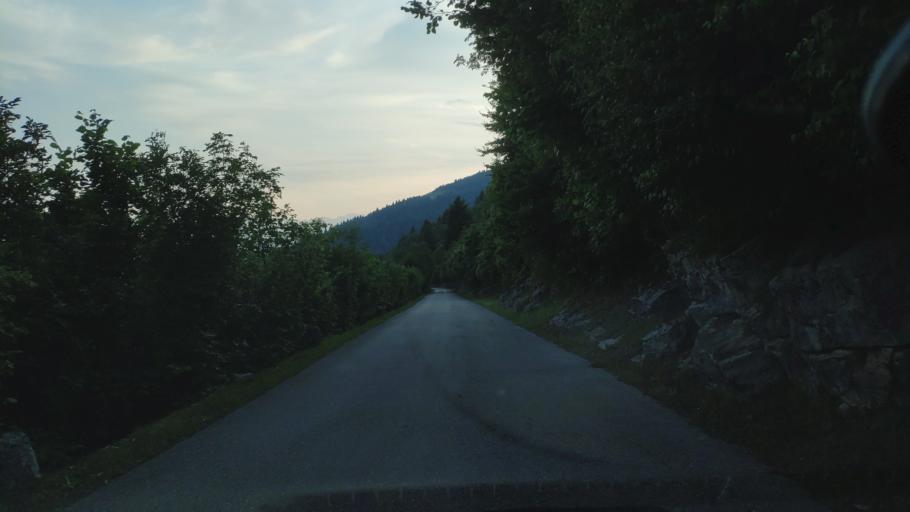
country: IT
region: Veneto
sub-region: Provincia di Vicenza
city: Calvene
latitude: 45.7898
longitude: 11.5192
